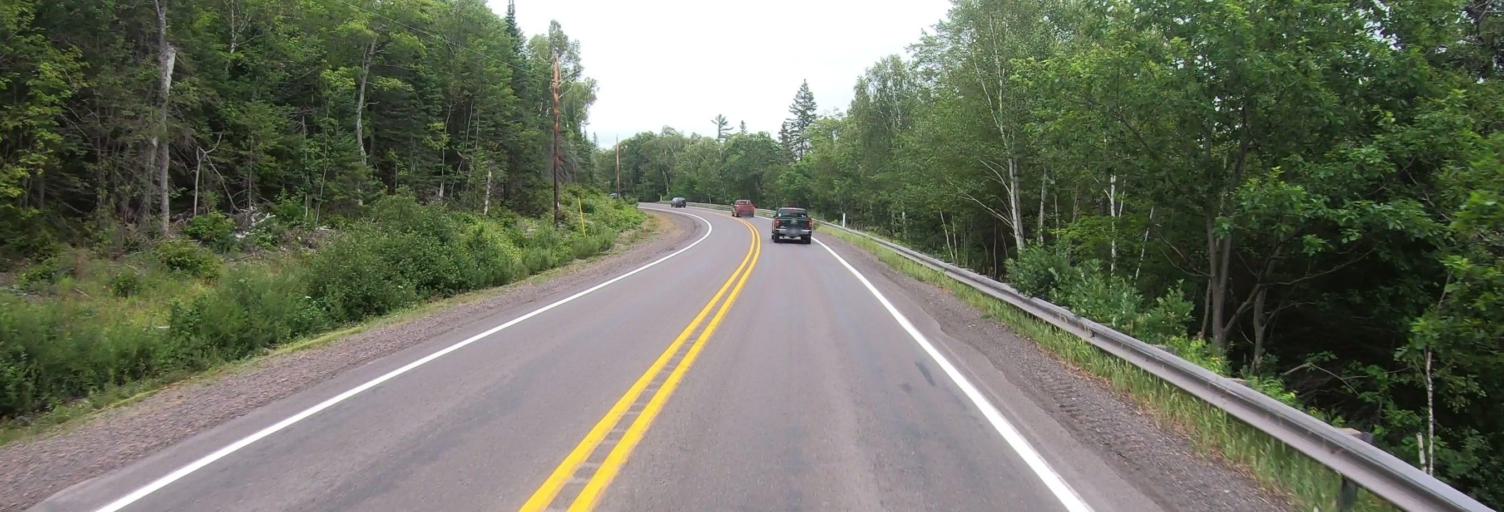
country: US
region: Michigan
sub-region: Keweenaw County
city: Eagle River
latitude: 47.4155
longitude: -88.1419
